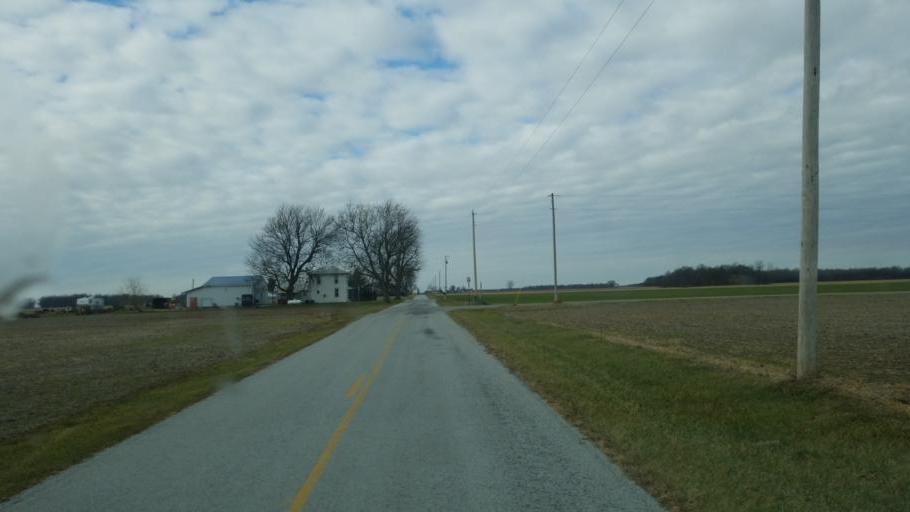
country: US
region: Ohio
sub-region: Hardin County
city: Forest
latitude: 40.6872
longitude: -83.4292
